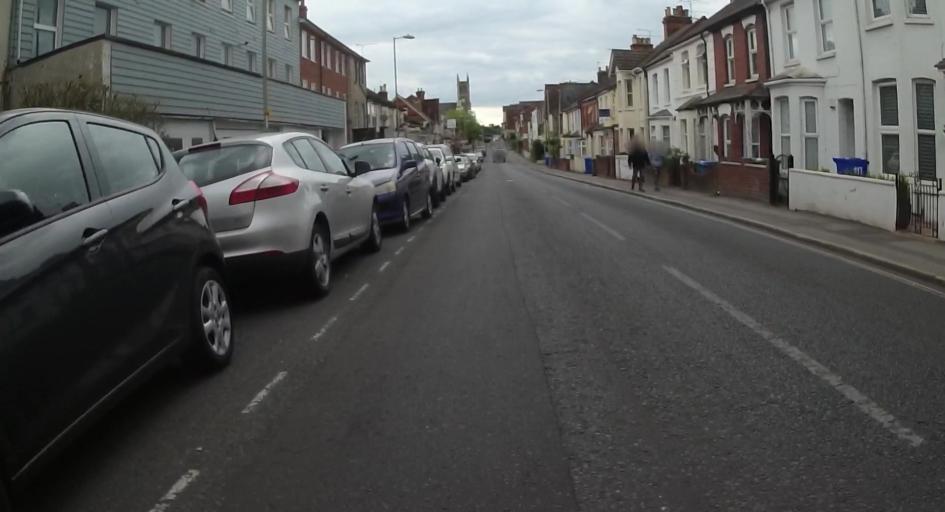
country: GB
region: England
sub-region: Hampshire
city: Aldershot
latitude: 51.2464
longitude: -0.7660
